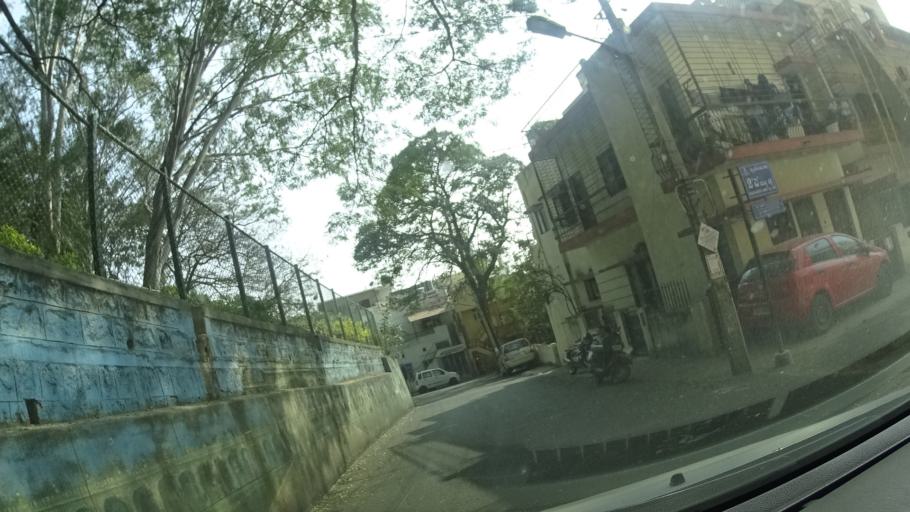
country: IN
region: Karnataka
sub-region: Bangalore Urban
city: Bangalore
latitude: 12.9446
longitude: 77.5624
